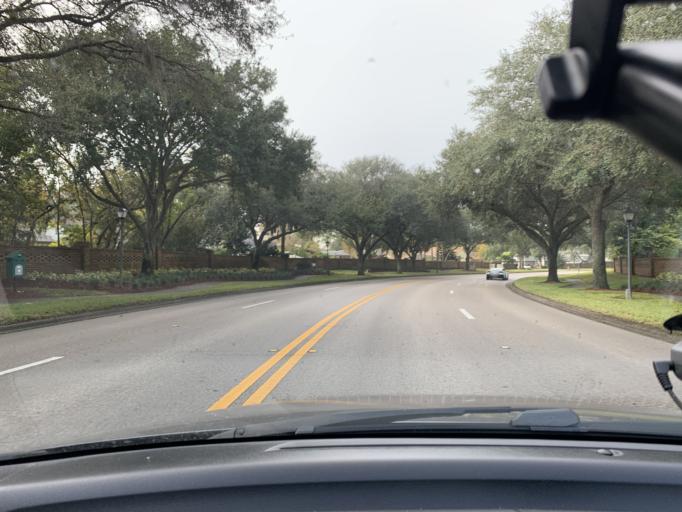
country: US
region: Florida
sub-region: Seminole County
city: Oviedo
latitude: 28.6487
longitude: -81.1985
